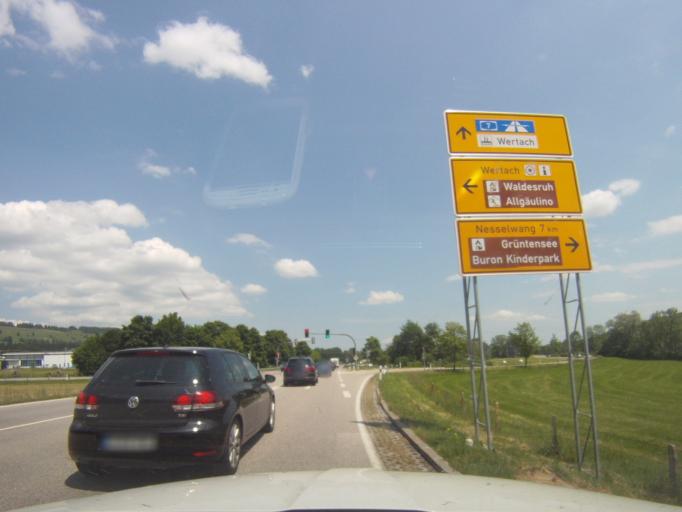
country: DE
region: Bavaria
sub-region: Swabia
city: Wertach
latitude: 47.6012
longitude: 10.4201
